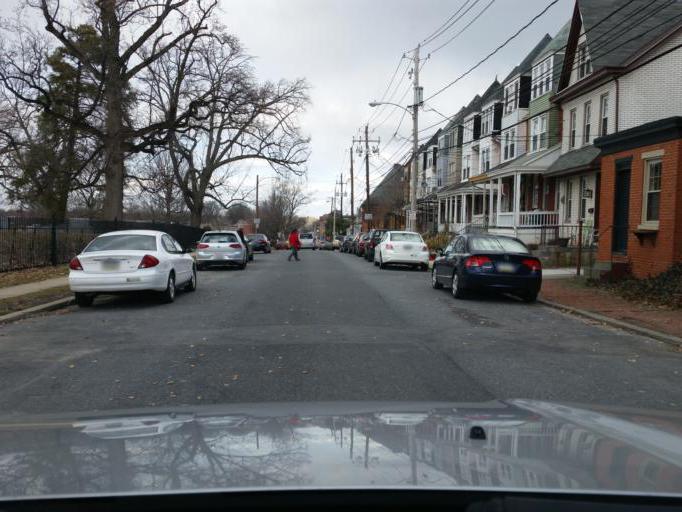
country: US
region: Pennsylvania
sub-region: Lancaster County
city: Lancaster
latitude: 40.0441
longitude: -76.2999
